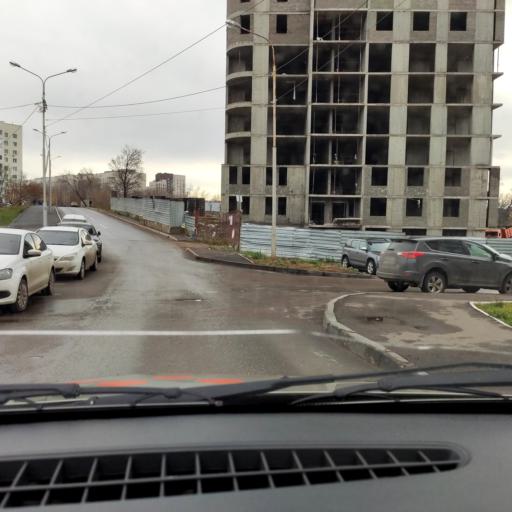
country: RU
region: Bashkortostan
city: Ufa
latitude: 54.7825
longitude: 56.0151
